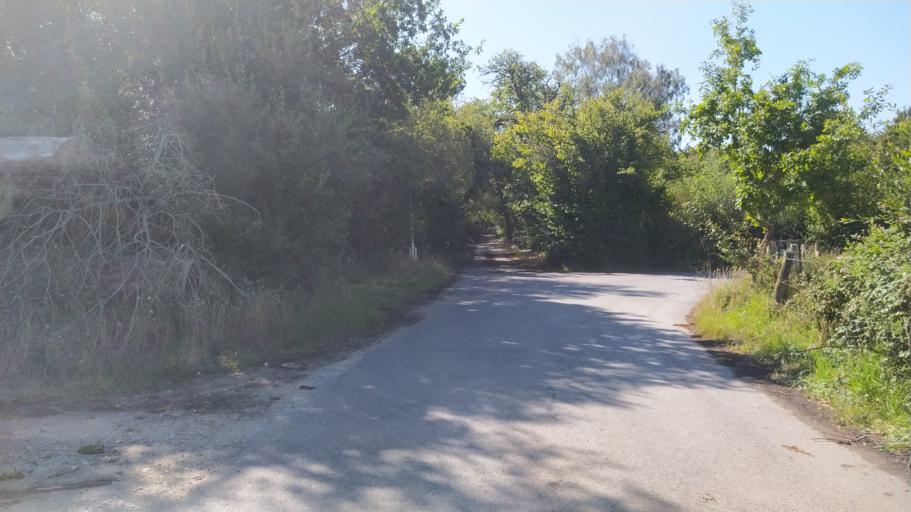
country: GB
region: England
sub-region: Dorset
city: Wareham
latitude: 50.6668
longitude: -2.1469
